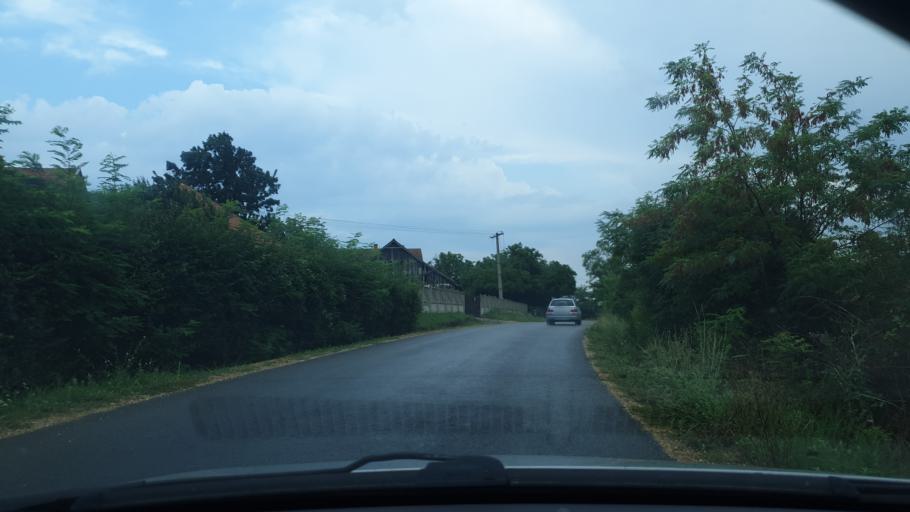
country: RS
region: Central Serbia
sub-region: Sumadijski Okrug
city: Kragujevac
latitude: 44.0653
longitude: 20.7909
